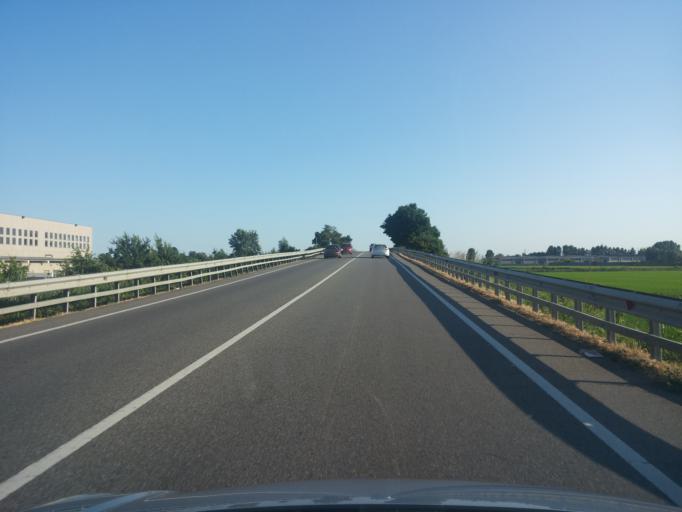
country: IT
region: Piedmont
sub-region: Provincia di Vercelli
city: Caresanablot
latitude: 45.3306
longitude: 8.3903
